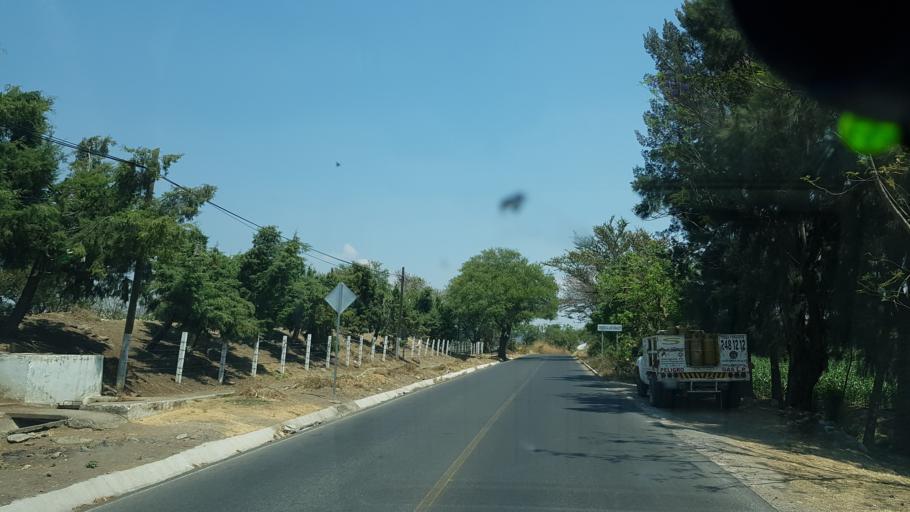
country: MX
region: Puebla
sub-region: Huaquechula
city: Cacaloxuchitl
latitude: 18.7896
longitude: -98.4746
